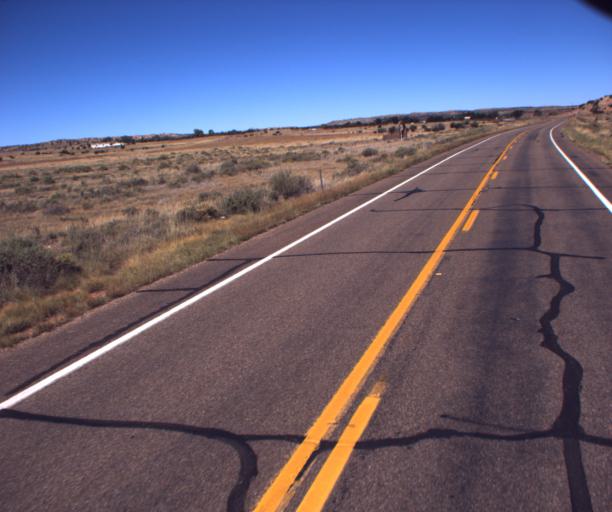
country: US
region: Arizona
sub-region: Apache County
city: Saint Johns
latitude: 34.4223
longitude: -109.4112
